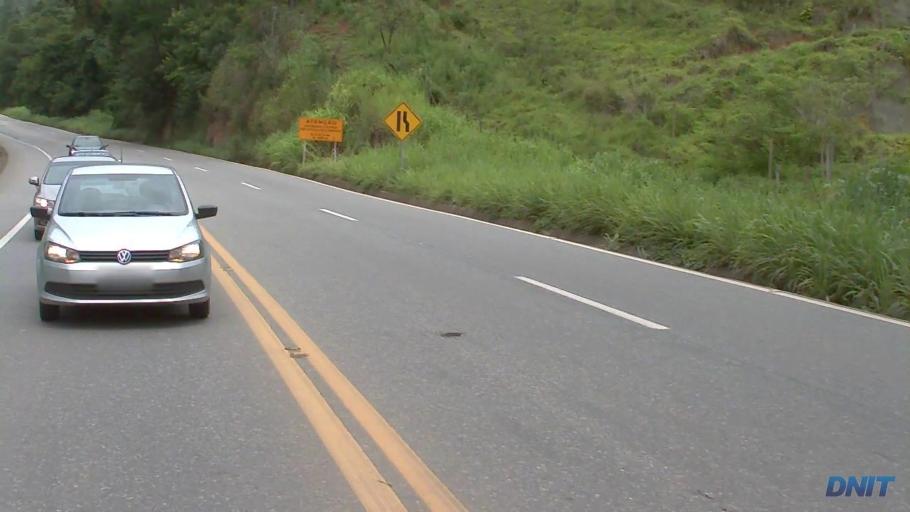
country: BR
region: Minas Gerais
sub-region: Nova Era
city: Nova Era
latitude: -19.7280
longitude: -43.0130
